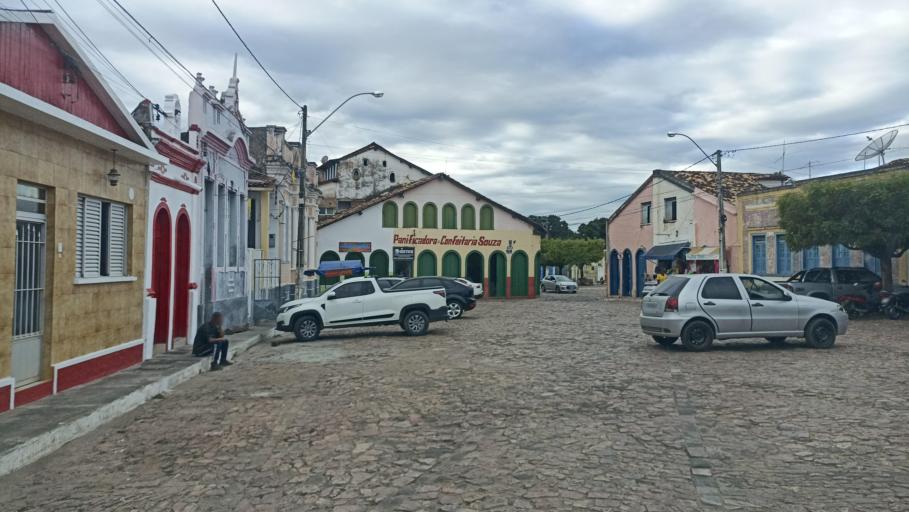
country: BR
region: Bahia
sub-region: Andarai
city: Vera Cruz
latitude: -12.8082
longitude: -41.3321
